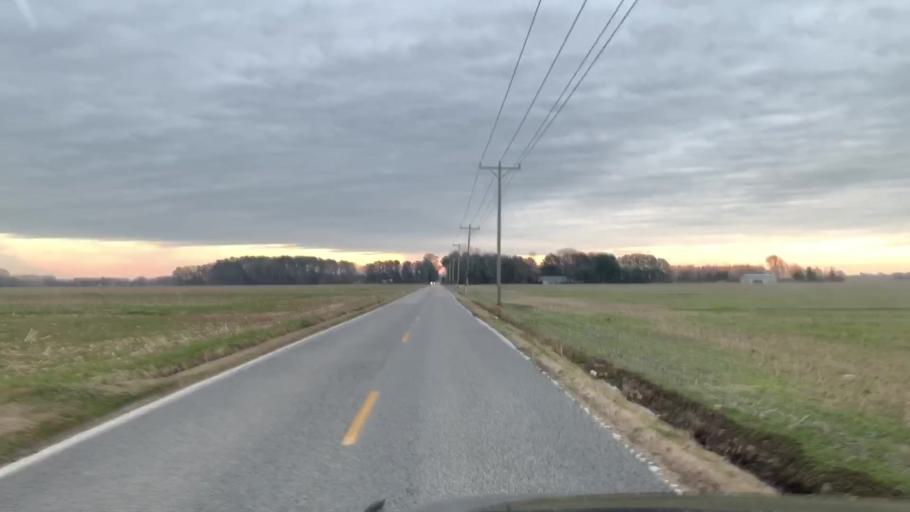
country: US
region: North Carolina
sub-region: Currituck County
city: Moyock
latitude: 36.6340
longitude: -76.1861
